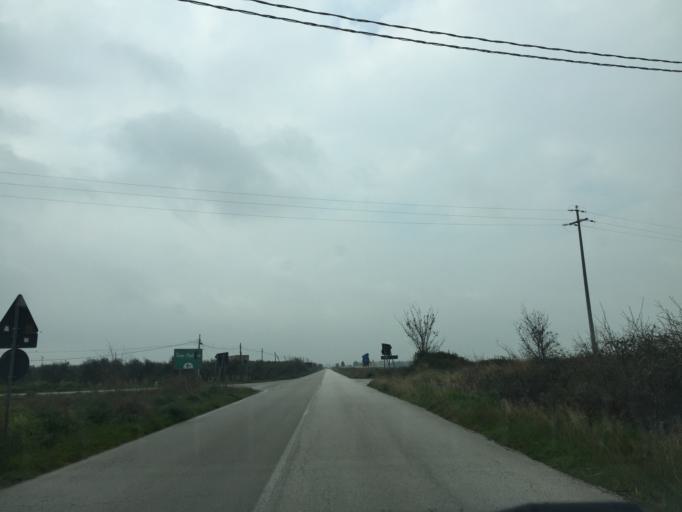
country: IT
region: Apulia
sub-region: Provincia di Foggia
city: Castelluccio dei Sauri
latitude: 41.4001
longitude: 15.4284
